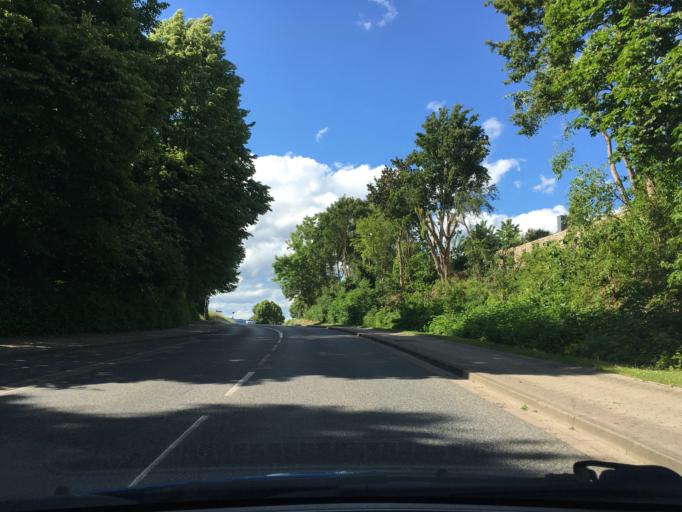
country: DE
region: Lower Saxony
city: Bovenden
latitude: 51.5892
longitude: 9.8708
